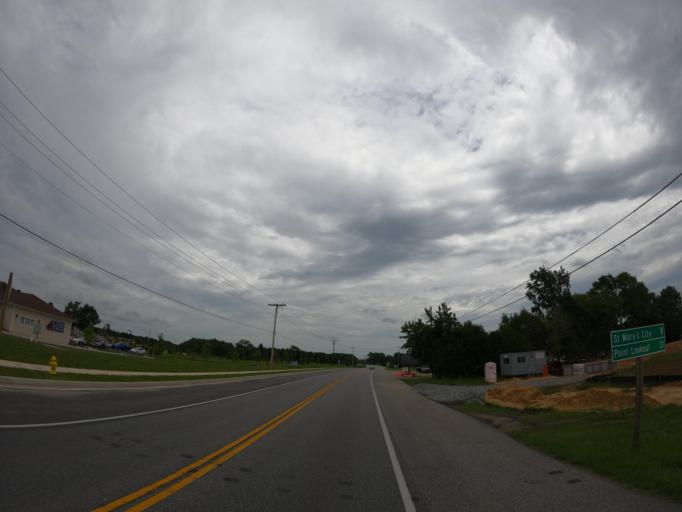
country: US
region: Maryland
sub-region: Saint Mary's County
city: California
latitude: 38.2383
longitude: -76.5197
